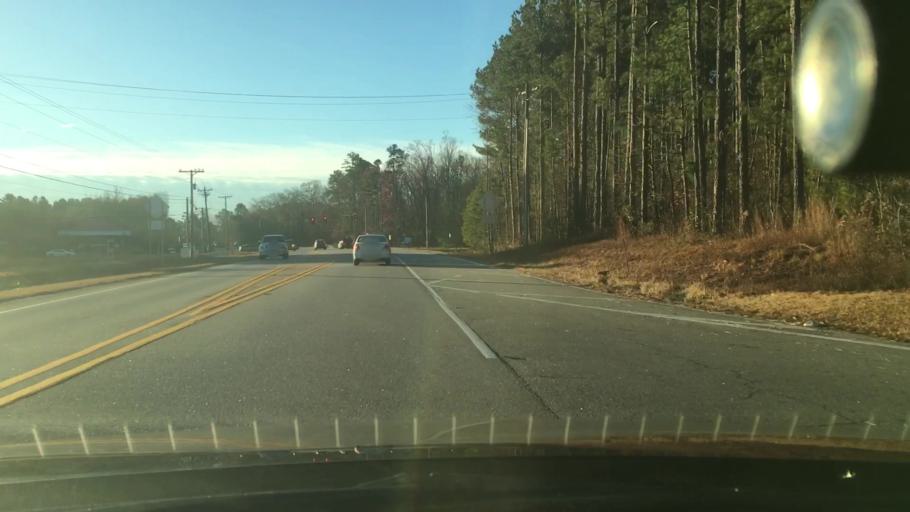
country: US
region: Georgia
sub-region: Fayette County
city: Peachtree City
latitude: 33.3611
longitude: -84.6621
